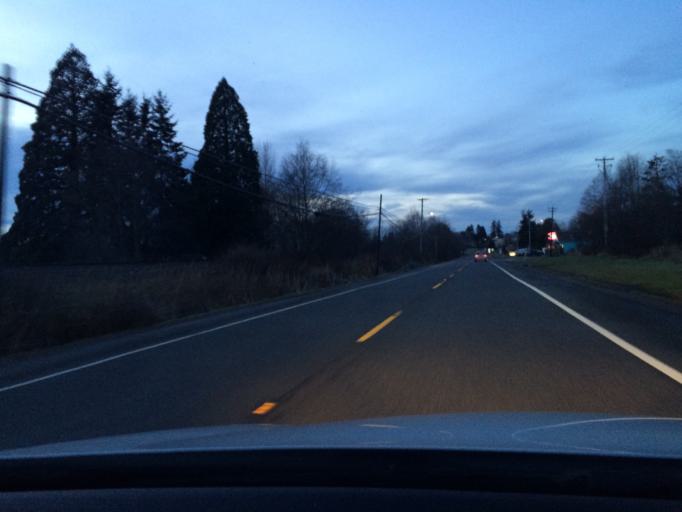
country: US
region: Washington
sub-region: Whatcom County
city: Blaine
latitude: 48.9811
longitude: -122.7364
